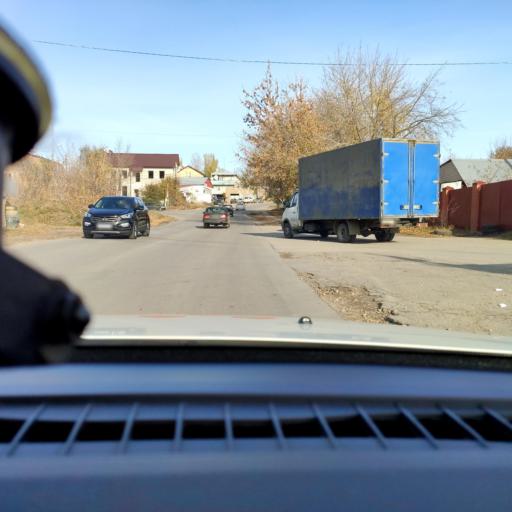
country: RU
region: Samara
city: Samara
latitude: 53.1800
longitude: 50.1573
